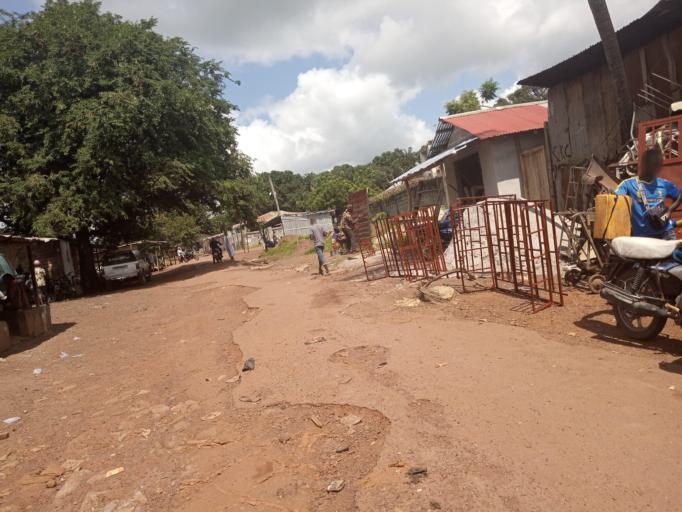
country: SL
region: Northern Province
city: Kamakwie
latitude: 9.4977
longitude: -12.2410
